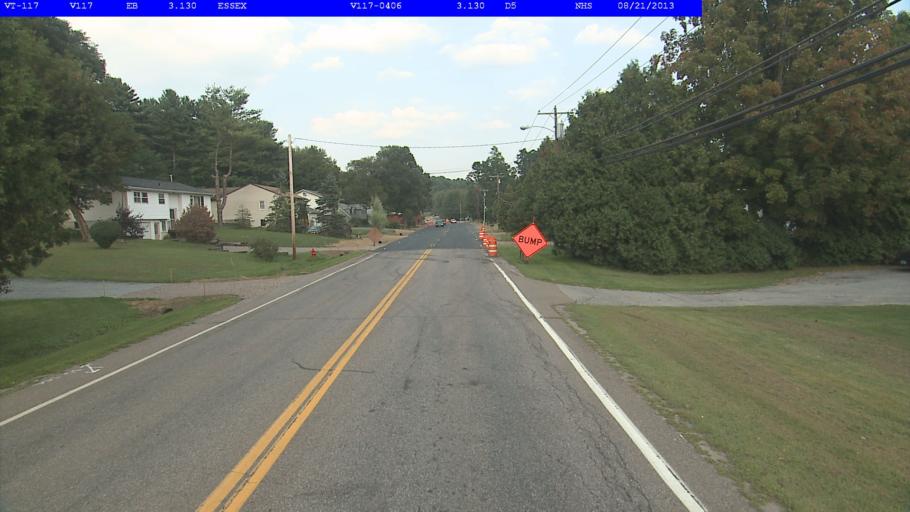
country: US
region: Vermont
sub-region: Chittenden County
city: Williston
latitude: 44.4790
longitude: -73.0523
